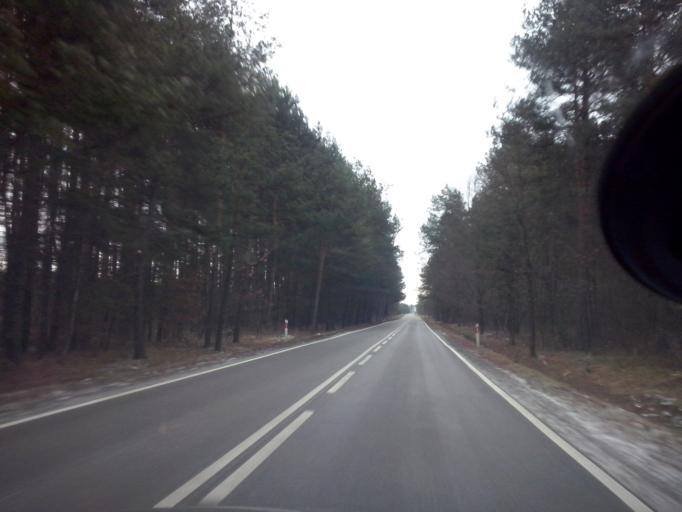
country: PL
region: Lublin Voivodeship
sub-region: Powiat bilgorajski
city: Biszcza
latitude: 50.4986
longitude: 22.6118
